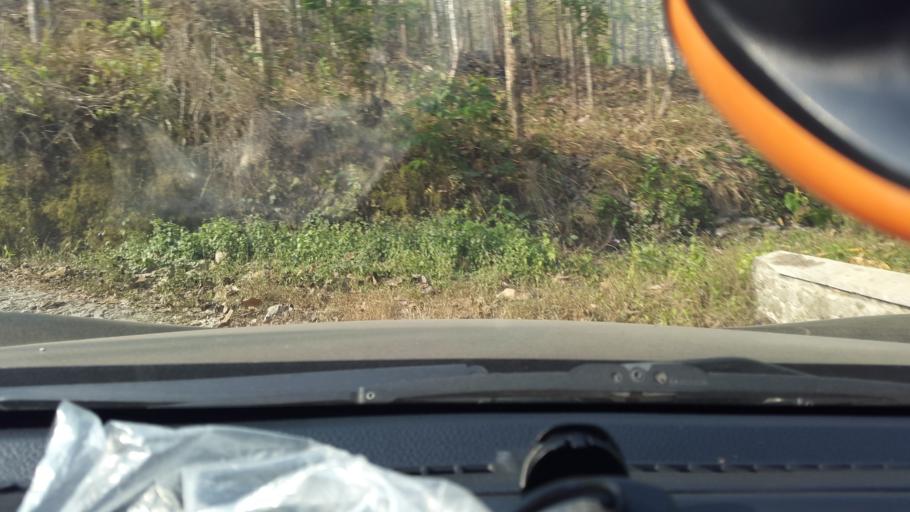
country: ID
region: West Java
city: Cikupa
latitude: -7.3597
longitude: 106.7043
